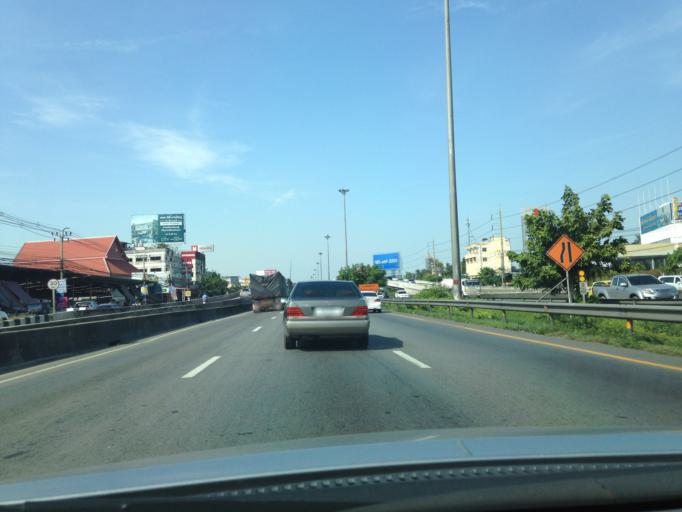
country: TH
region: Nonthaburi
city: Bang Yai
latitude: 13.8572
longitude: 100.4114
